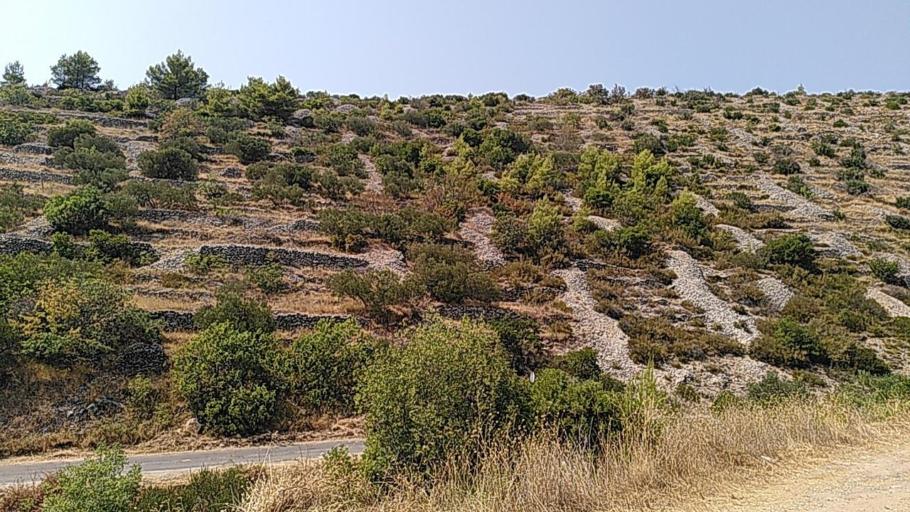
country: HR
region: Splitsko-Dalmatinska
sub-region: Grad Hvar
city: Hvar
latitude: 43.1697
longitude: 16.5127
